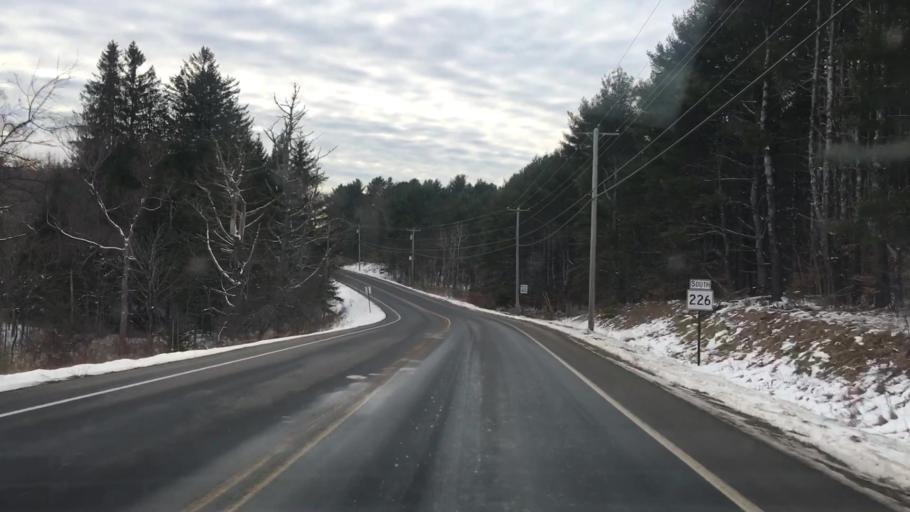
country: US
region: Maine
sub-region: Kennebec County
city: Chelsea
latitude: 44.2719
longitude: -69.6937
